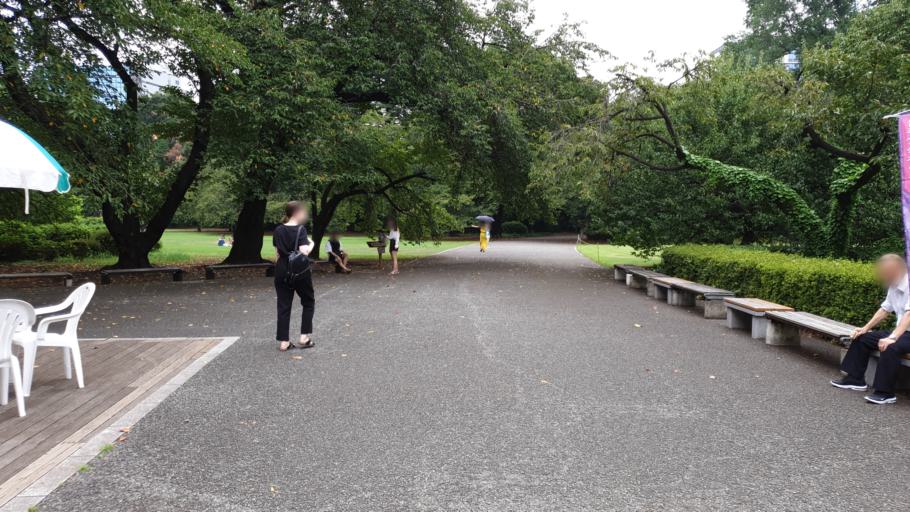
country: JP
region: Tokyo
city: Tokyo
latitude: 35.6869
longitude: 139.7083
